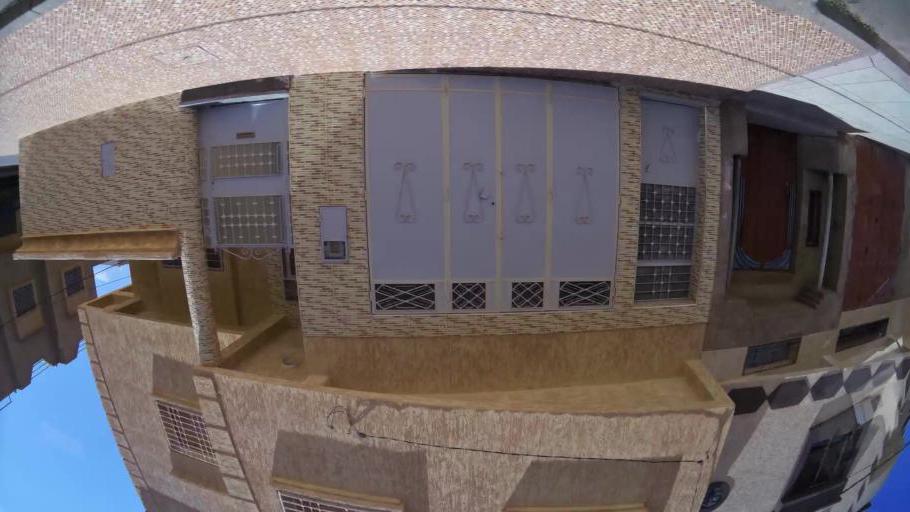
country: MA
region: Oriental
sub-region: Oujda-Angad
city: Oujda
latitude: 34.6938
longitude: -1.8891
